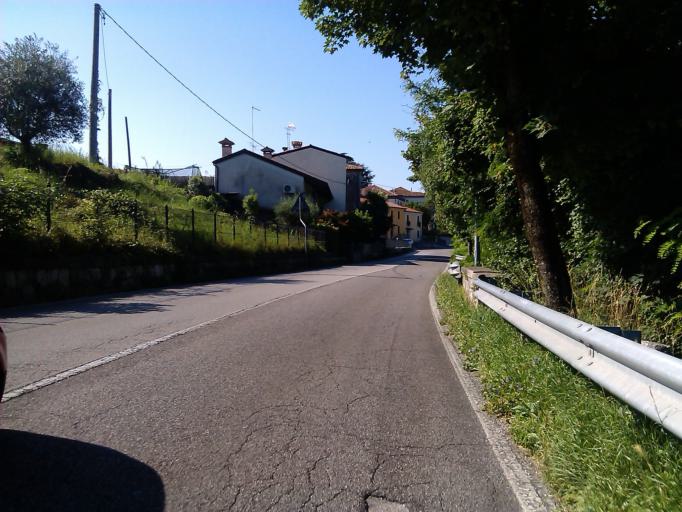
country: IT
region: Veneto
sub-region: Provincia di Vicenza
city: Bassano del Grappa
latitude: 45.7776
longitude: 11.7421
